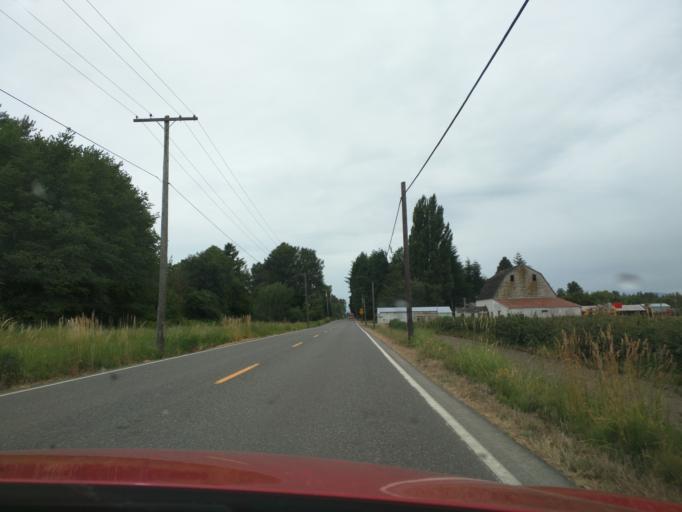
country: US
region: Washington
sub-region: Whatcom County
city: Everson
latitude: 48.8882
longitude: -122.3205
